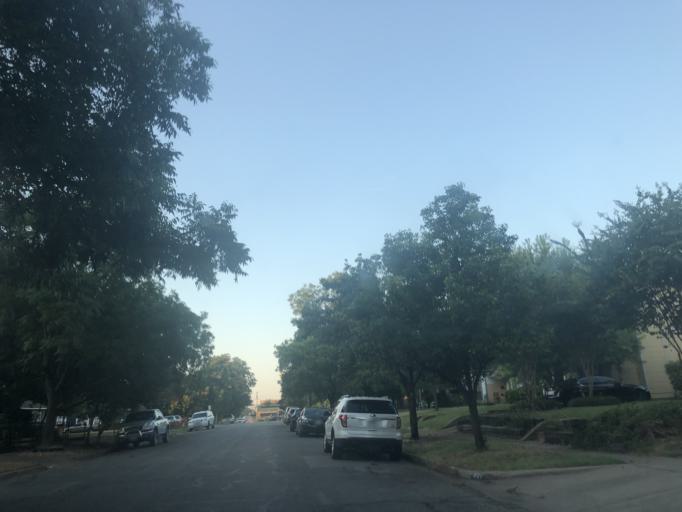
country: US
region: Texas
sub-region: Dallas County
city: Dallas
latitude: 32.7515
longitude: -96.8266
